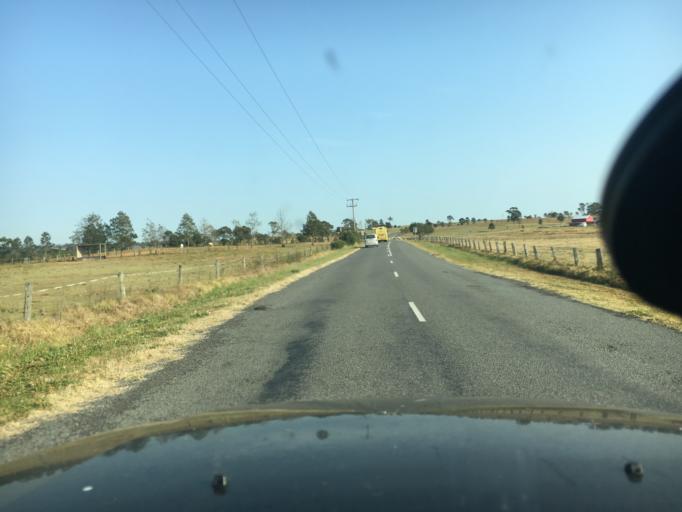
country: AU
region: New South Wales
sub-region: Cessnock
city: Branxton
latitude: -32.6005
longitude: 151.3352
